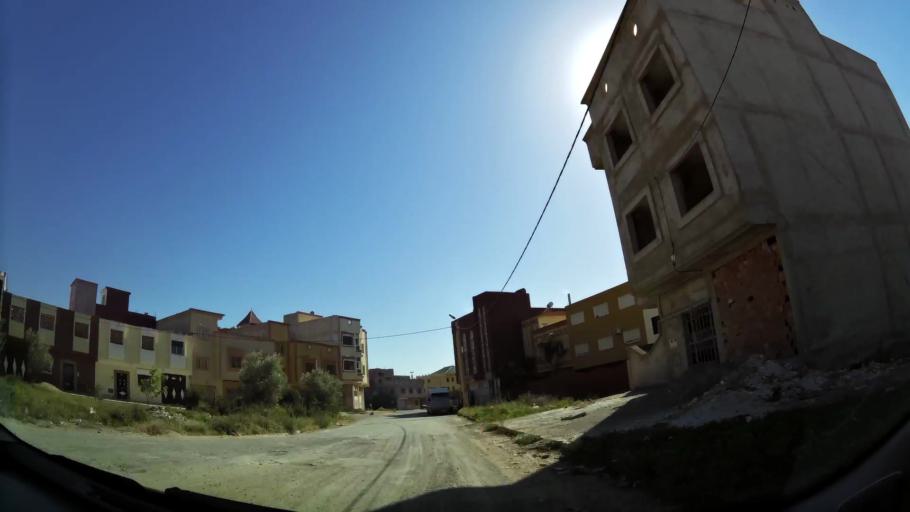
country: MA
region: Oriental
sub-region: Berkane-Taourirt
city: Berkane
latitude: 34.9399
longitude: -2.3385
